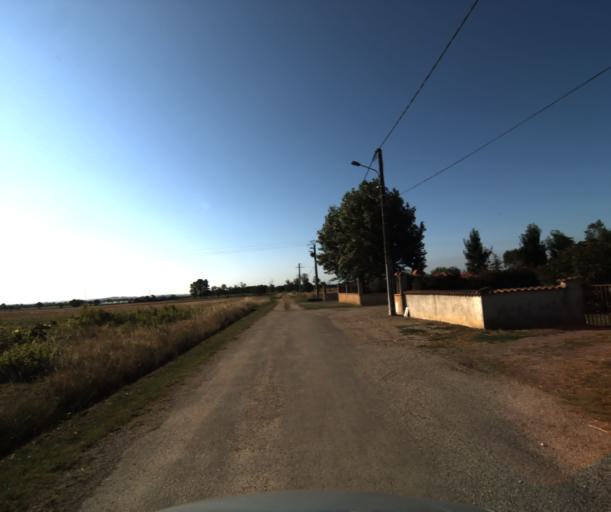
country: FR
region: Midi-Pyrenees
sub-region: Departement de la Haute-Garonne
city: Muret
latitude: 43.4492
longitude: 1.3714
